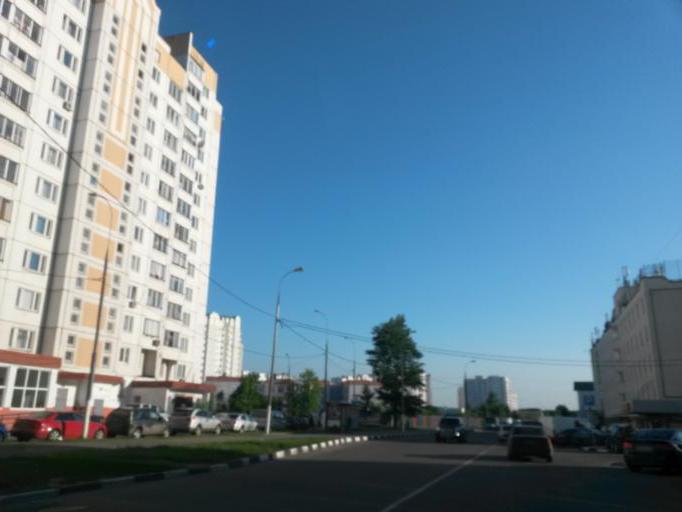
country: RU
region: Moskovskaya
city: Shcherbinka
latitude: 55.5480
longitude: 37.5664
